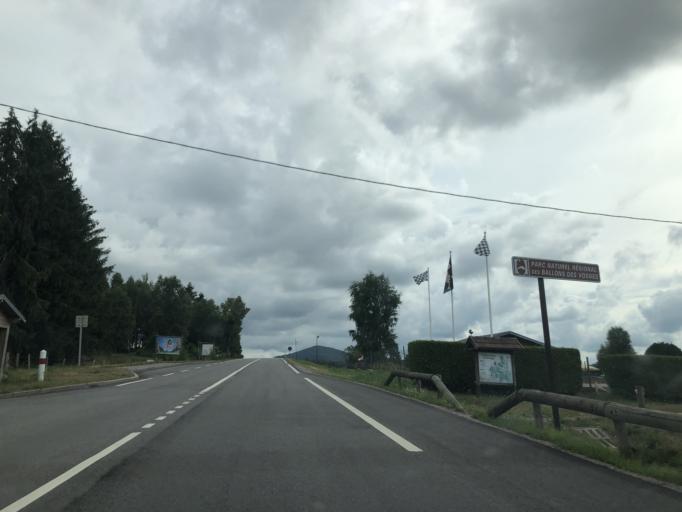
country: FR
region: Lorraine
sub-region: Departement des Vosges
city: Anould
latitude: 48.1655
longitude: 6.9187
